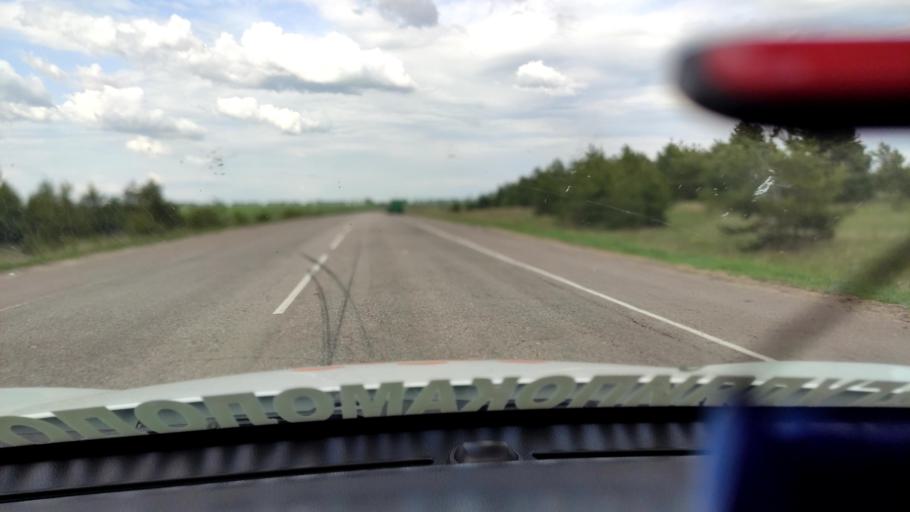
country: RU
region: Voronezj
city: Kolodeznyy
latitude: 51.3816
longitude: 39.2183
